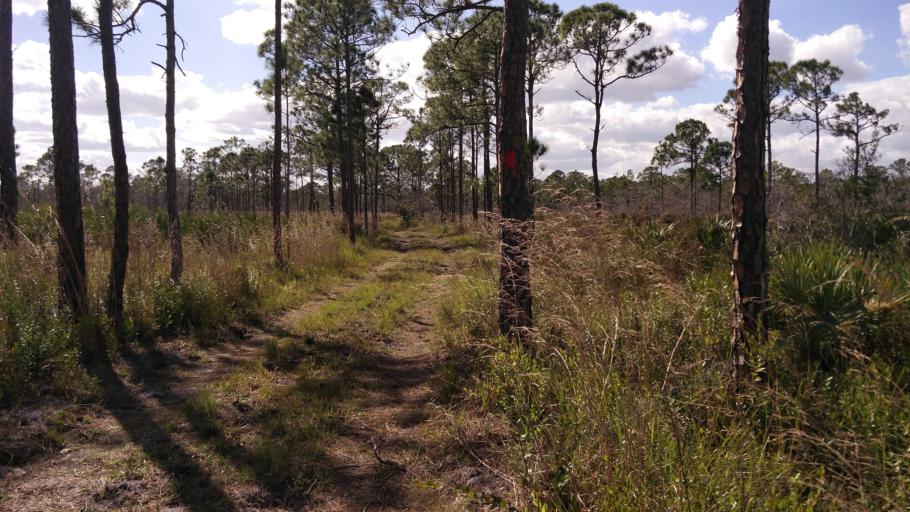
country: US
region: Florida
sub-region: Martin County
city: Hobe Sound
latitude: 27.0197
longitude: -80.1506
